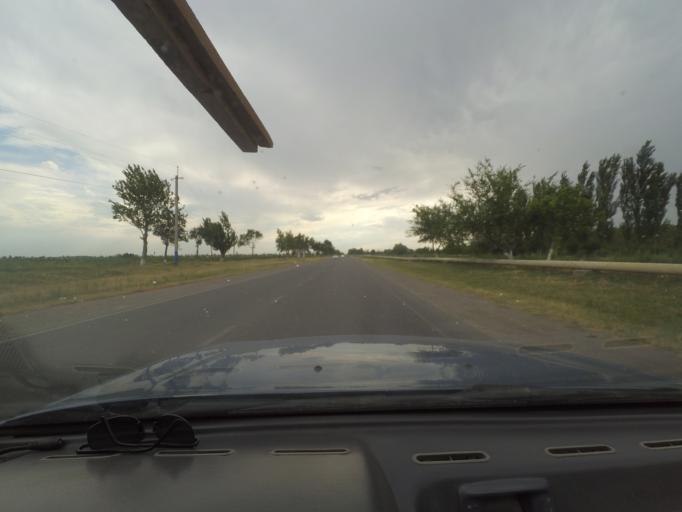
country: UZ
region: Sirdaryo
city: Guliston
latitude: 40.4920
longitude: 68.8362
